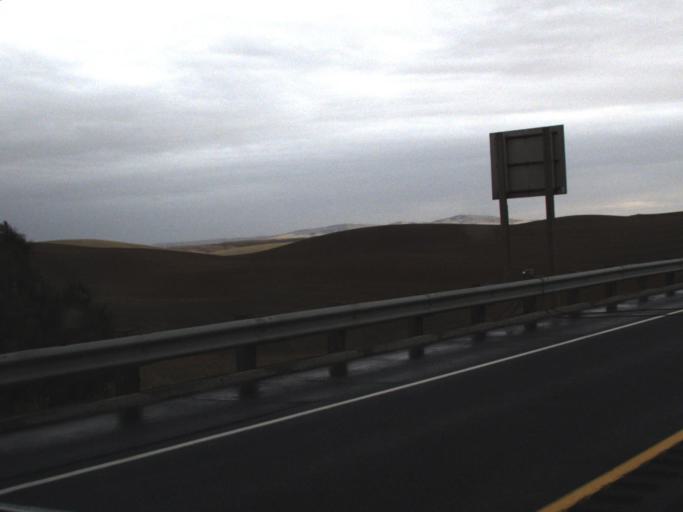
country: US
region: Washington
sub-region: Whitman County
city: Pullman
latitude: 46.7188
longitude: -117.2201
